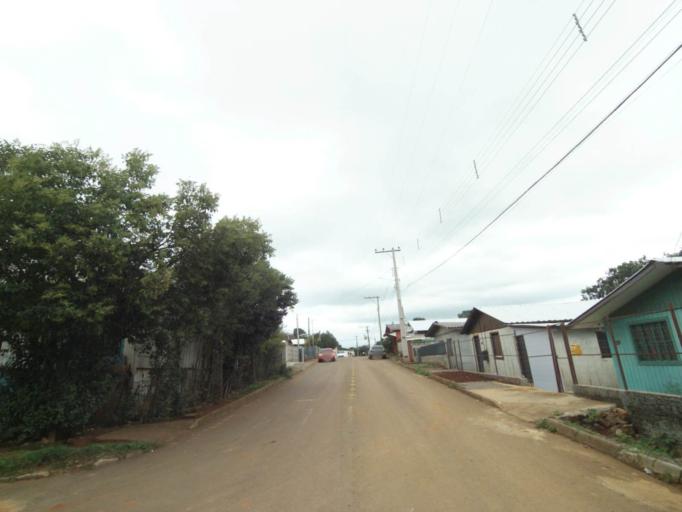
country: BR
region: Rio Grande do Sul
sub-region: Lagoa Vermelha
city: Lagoa Vermelha
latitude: -28.2024
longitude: -51.5314
